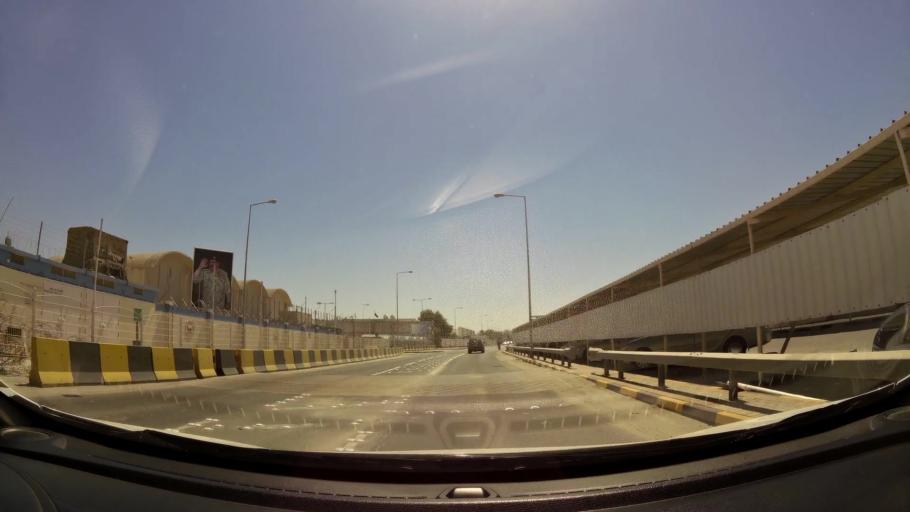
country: BH
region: Muharraq
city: Al Muharraq
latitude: 26.2710
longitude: 50.6148
